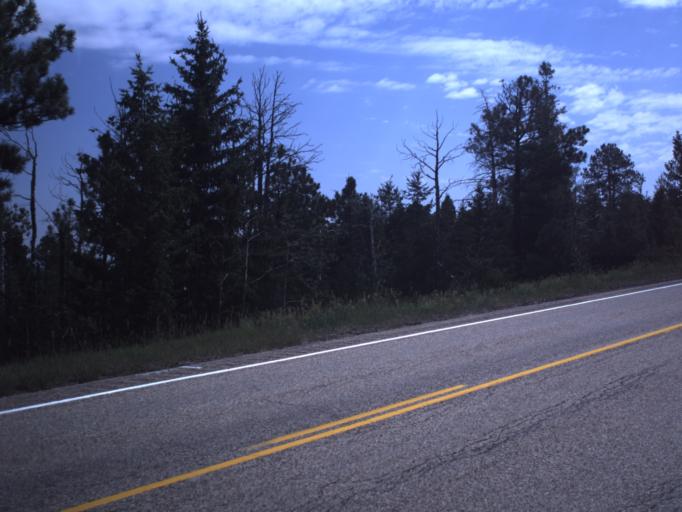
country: US
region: Utah
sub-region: Daggett County
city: Manila
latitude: 40.8617
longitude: -109.4759
